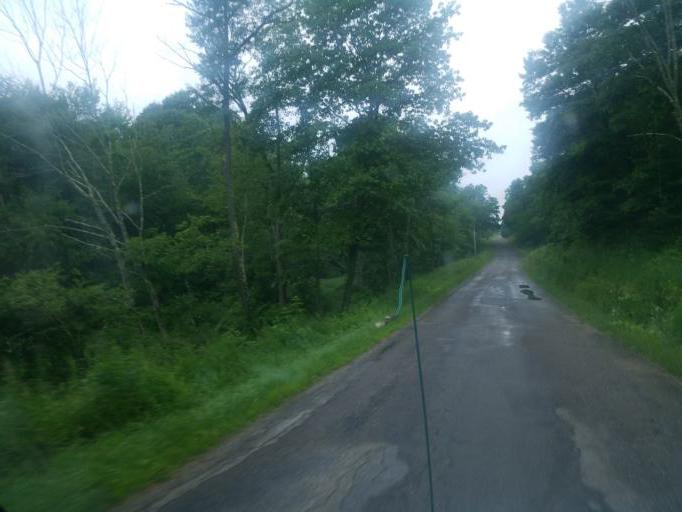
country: US
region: Ohio
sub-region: Columbiana County
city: Salineville
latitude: 40.6040
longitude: -80.9097
